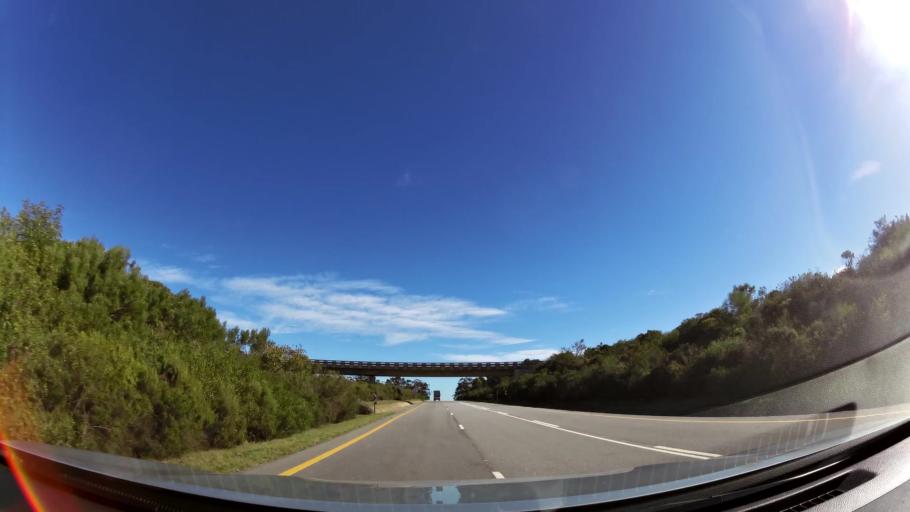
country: ZA
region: Eastern Cape
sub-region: Cacadu District Municipality
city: Kruisfontein
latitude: -34.0186
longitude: 24.6215
